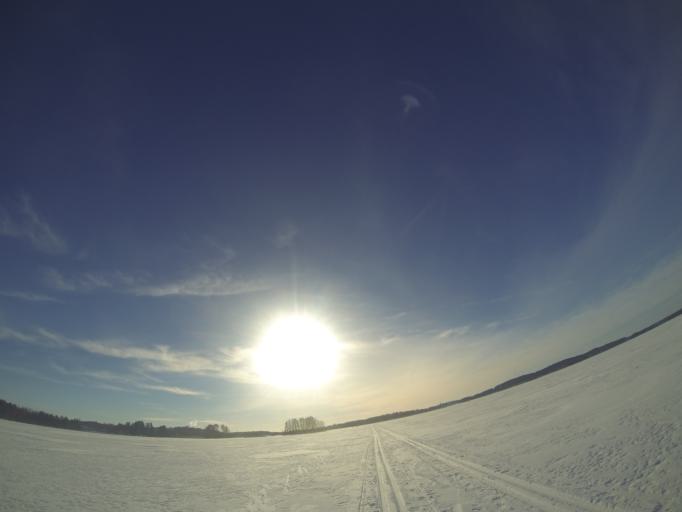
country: FI
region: Southern Savonia
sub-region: Savonlinna
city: Savonlinna
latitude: 61.8901
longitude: 28.9056
